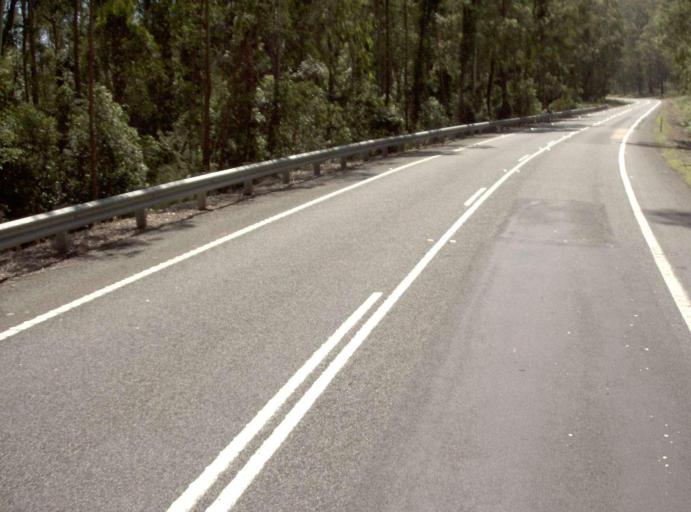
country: AU
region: New South Wales
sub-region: Bombala
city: Bombala
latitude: -37.5651
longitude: 149.0729
